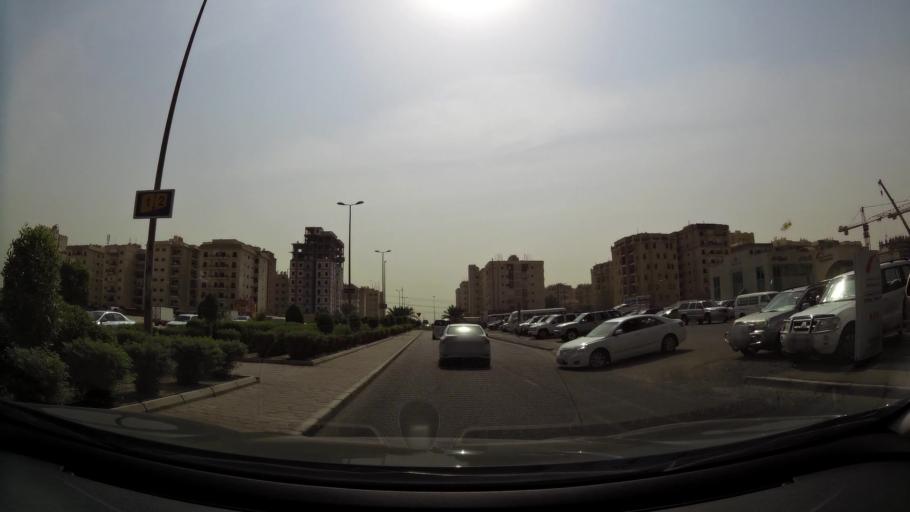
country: KW
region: Al Asimah
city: Ar Rabiyah
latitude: 29.3040
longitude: 47.9149
